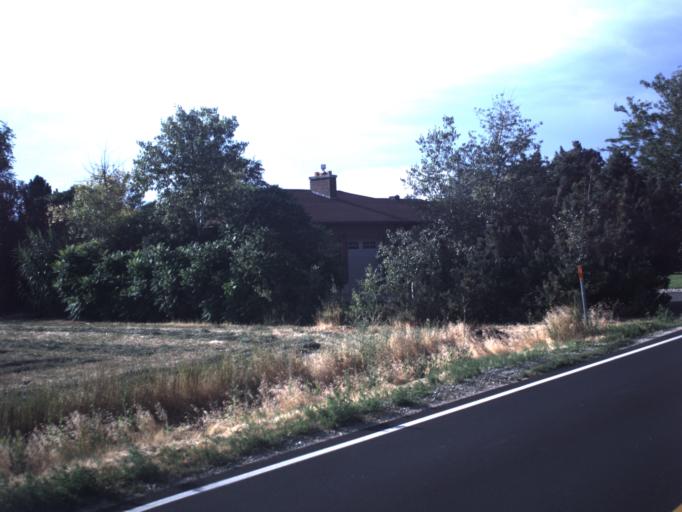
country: US
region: Utah
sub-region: Weber County
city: West Haven
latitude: 41.2378
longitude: -112.0927
